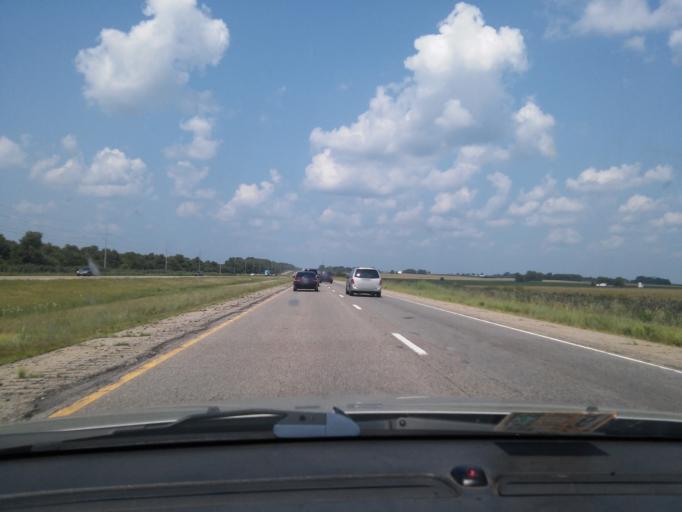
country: US
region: Illinois
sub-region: Logan County
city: Atlanta
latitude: 40.2253
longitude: -89.2724
